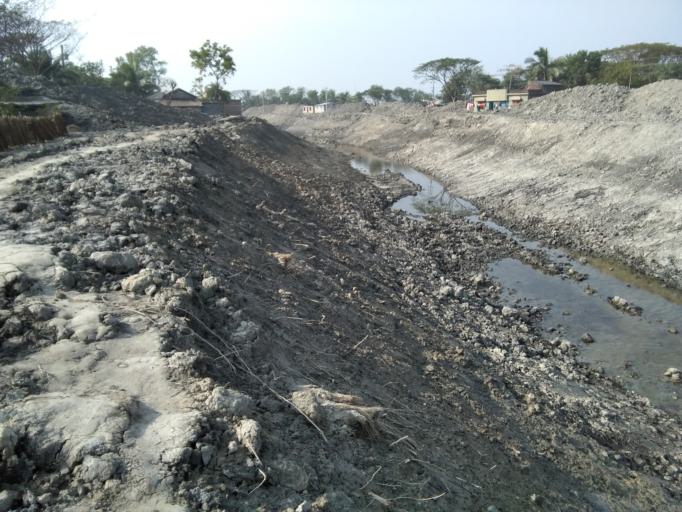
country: IN
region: West Bengal
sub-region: North 24 Parganas
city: Taki
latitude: 22.5909
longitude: 89.0348
